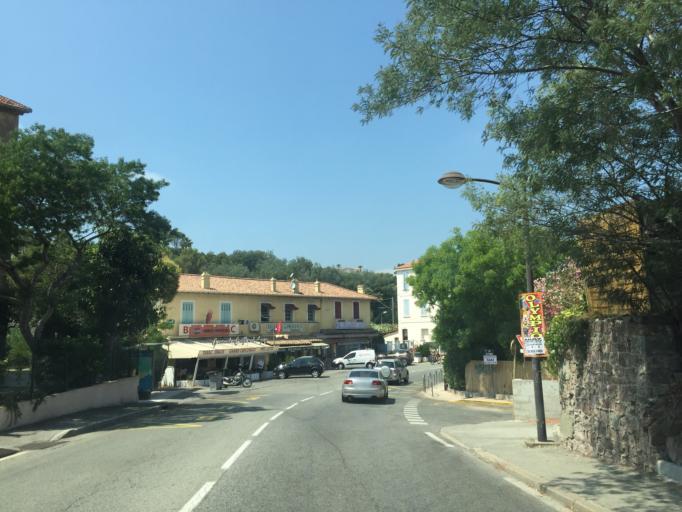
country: FR
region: Provence-Alpes-Cote d'Azur
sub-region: Departement du Var
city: Saint-Raphael
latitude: 43.4287
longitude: 6.8567
